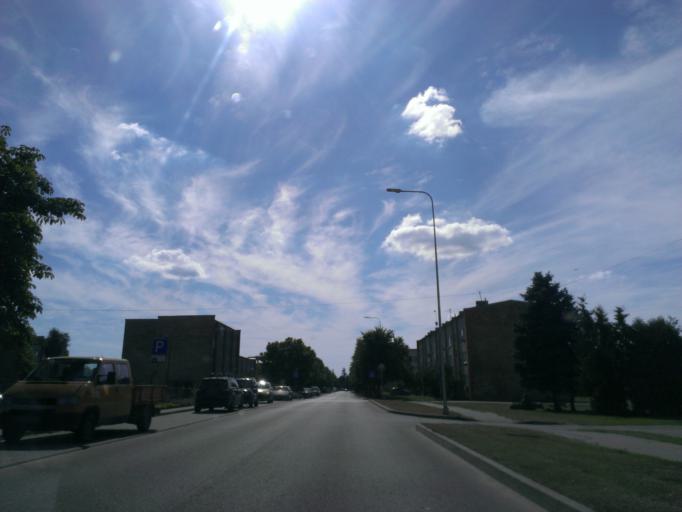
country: LV
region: Adazi
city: Adazi
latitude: 57.0803
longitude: 24.3214
